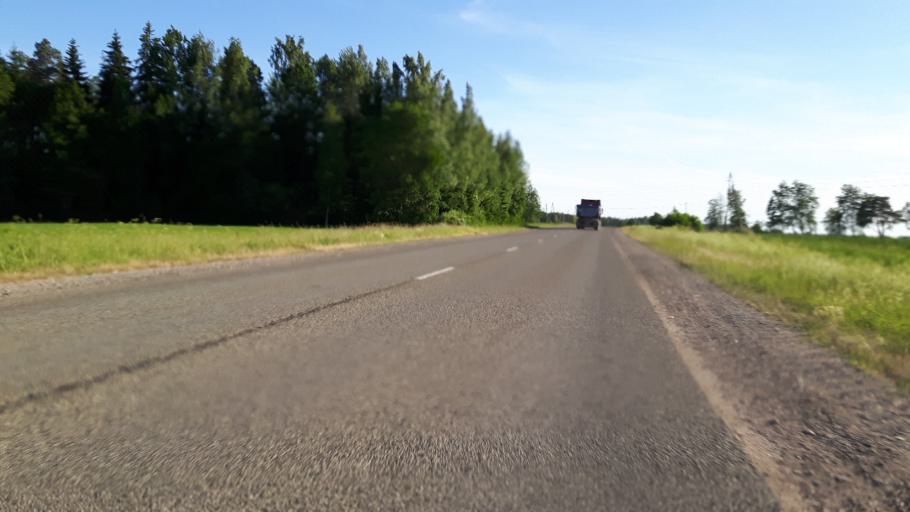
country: LV
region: Kuldigas Rajons
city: Kuldiga
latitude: 57.0321
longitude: 22.1999
